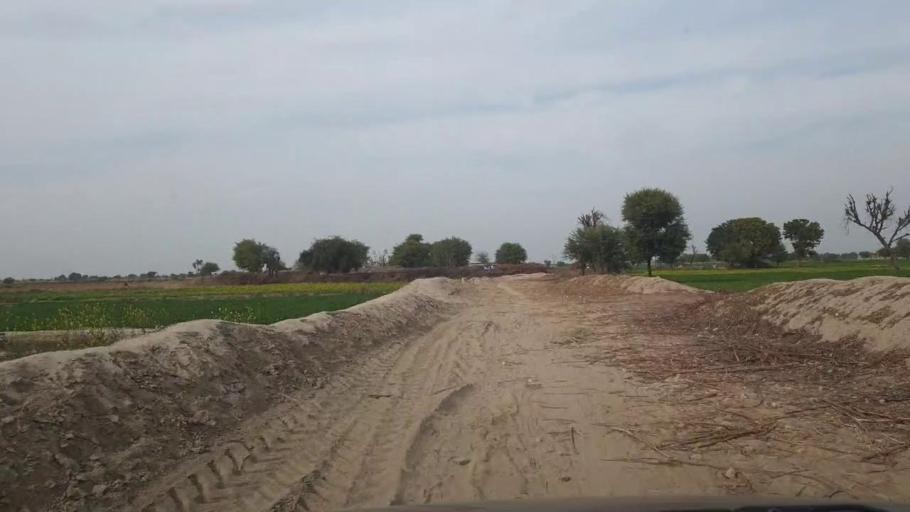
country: PK
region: Sindh
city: Shahpur Chakar
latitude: 26.1209
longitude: 68.5102
